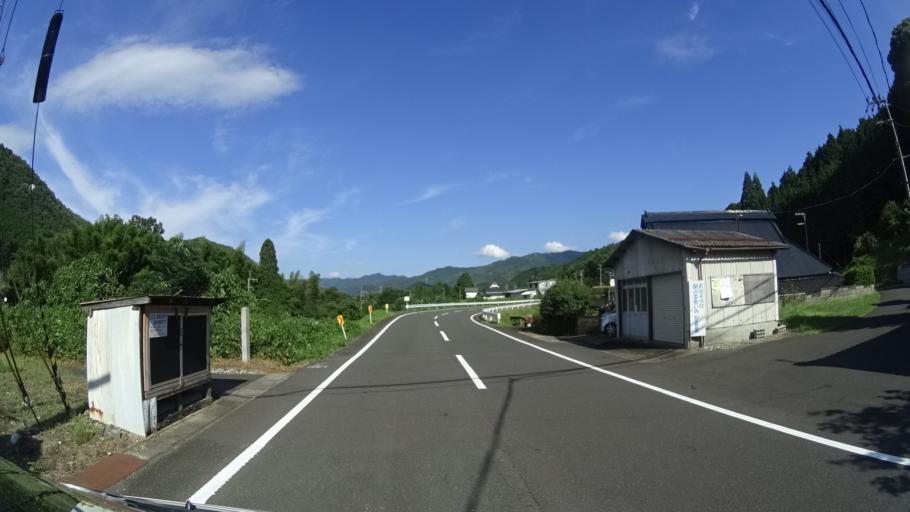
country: JP
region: Kyoto
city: Ayabe
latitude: 35.2881
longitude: 135.2790
